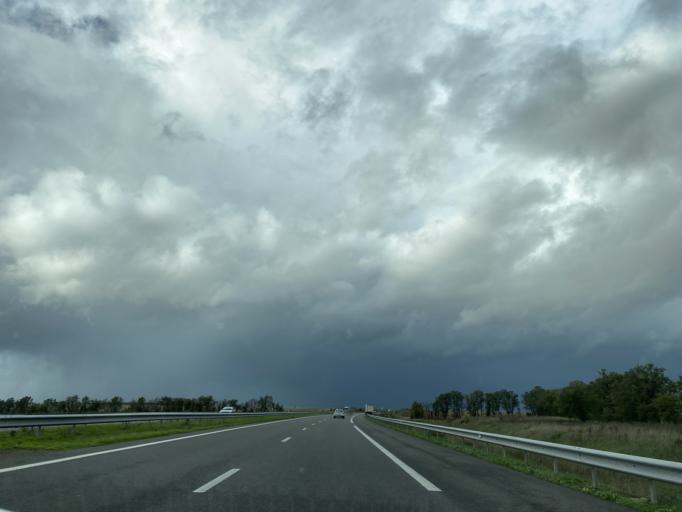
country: FR
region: Centre
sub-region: Departement du Cher
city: Plaimpied-Givaudins
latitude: 46.9881
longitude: 2.4111
